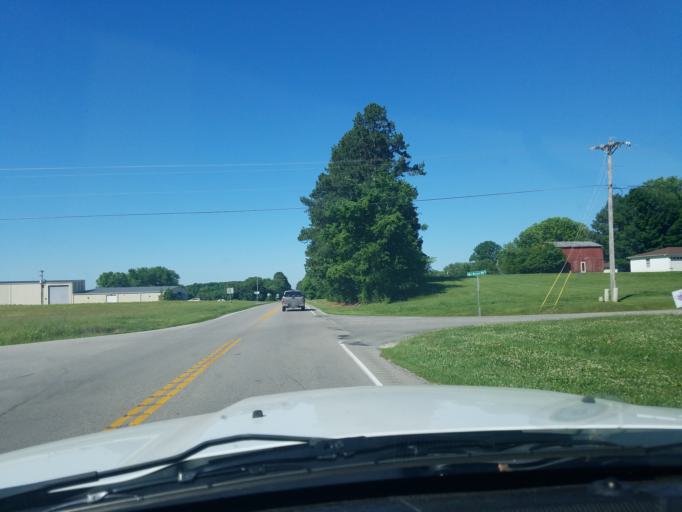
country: US
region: Kentucky
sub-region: Barren County
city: Glasgow
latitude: 36.9458
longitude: -85.9733
